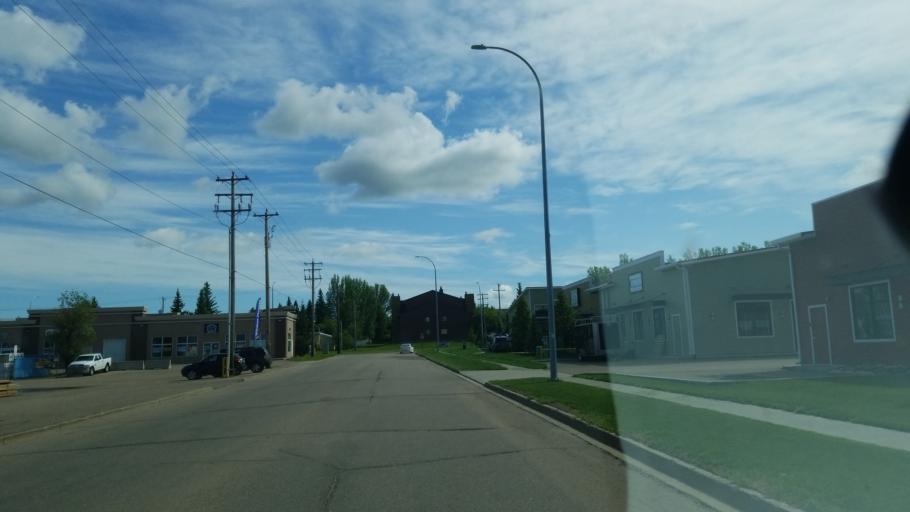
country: CA
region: Saskatchewan
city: Lloydminster
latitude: 53.2718
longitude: -110.0086
